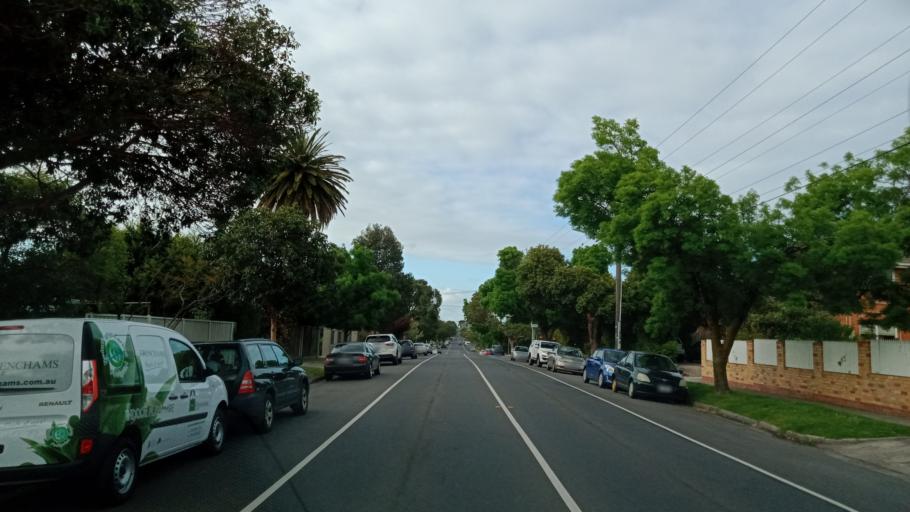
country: AU
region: Victoria
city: McKinnon
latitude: -37.9235
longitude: 145.0503
